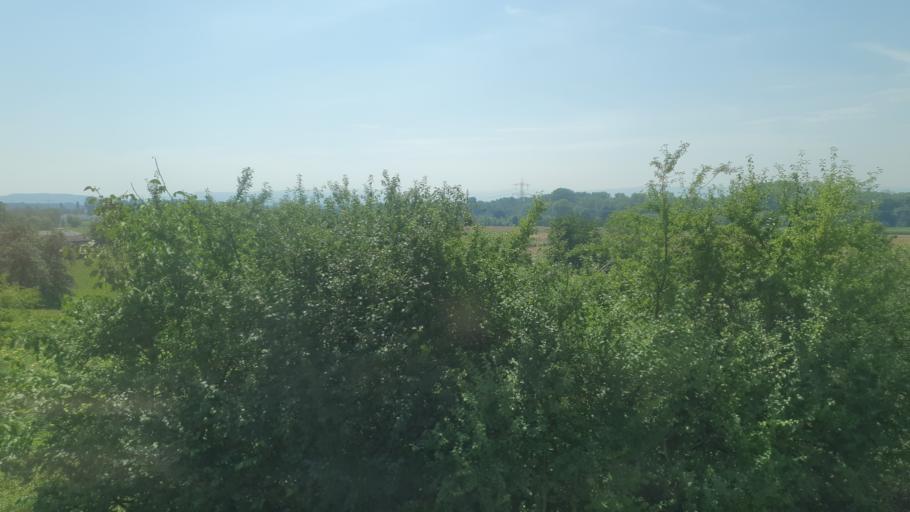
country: DE
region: Baden-Wuerttemberg
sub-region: Freiburg Region
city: Efringen-Kirchen
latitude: 47.6568
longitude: 7.5545
